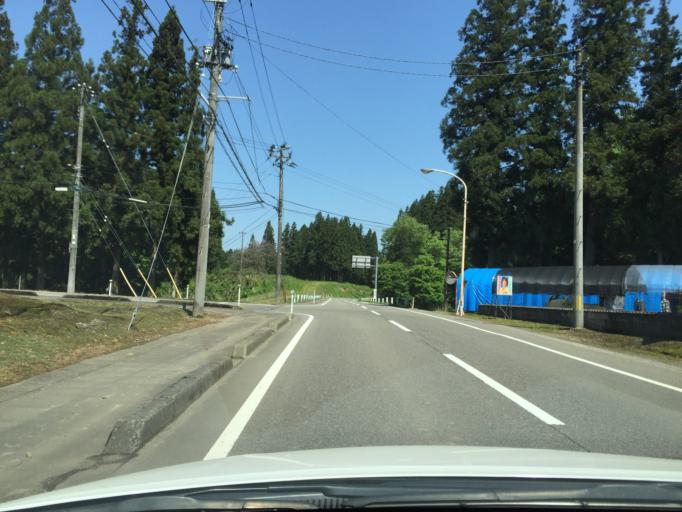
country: JP
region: Niigata
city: Kamo
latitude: 37.5791
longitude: 139.0725
